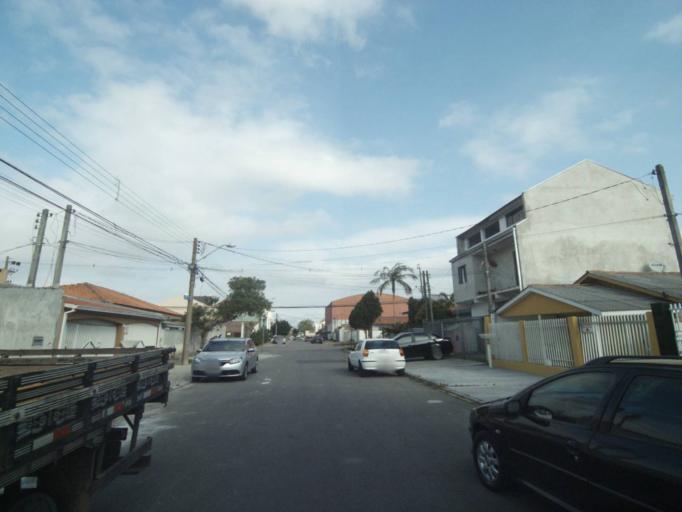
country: BR
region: Parana
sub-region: Sao Jose Dos Pinhais
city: Sao Jose dos Pinhais
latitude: -25.5388
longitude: -49.2611
